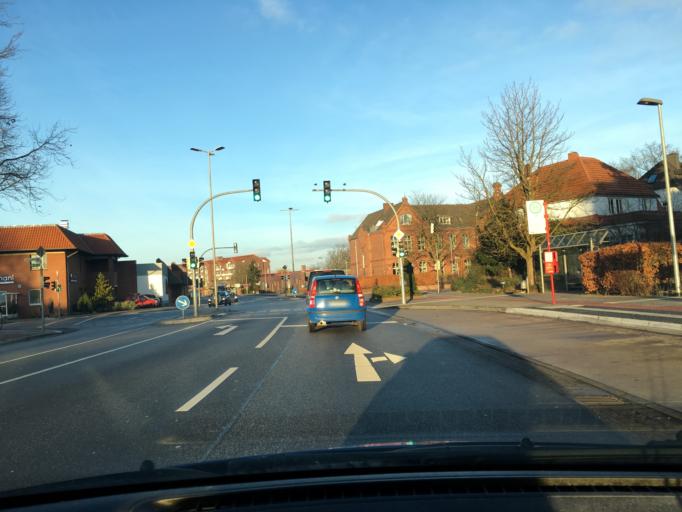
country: DE
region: Lower Saxony
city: Winsen
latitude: 53.3619
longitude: 10.2089
